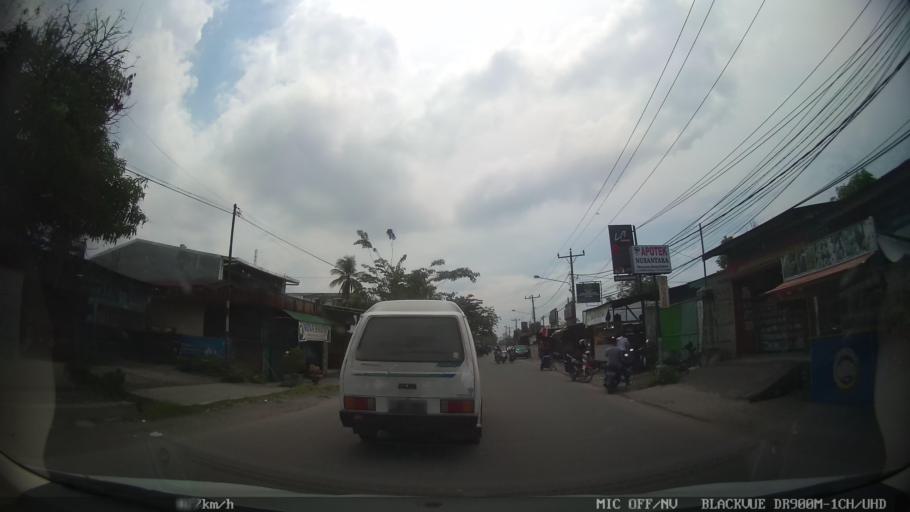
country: ID
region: North Sumatra
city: Medan
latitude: 3.6428
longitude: 98.6735
